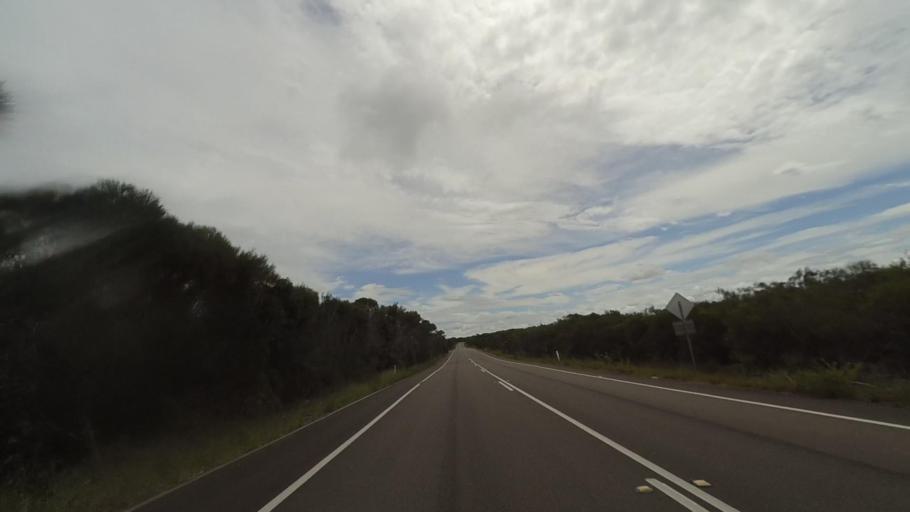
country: AU
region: New South Wales
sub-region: Sutherland Shire
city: Bundeena
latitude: -34.1026
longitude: 151.1180
